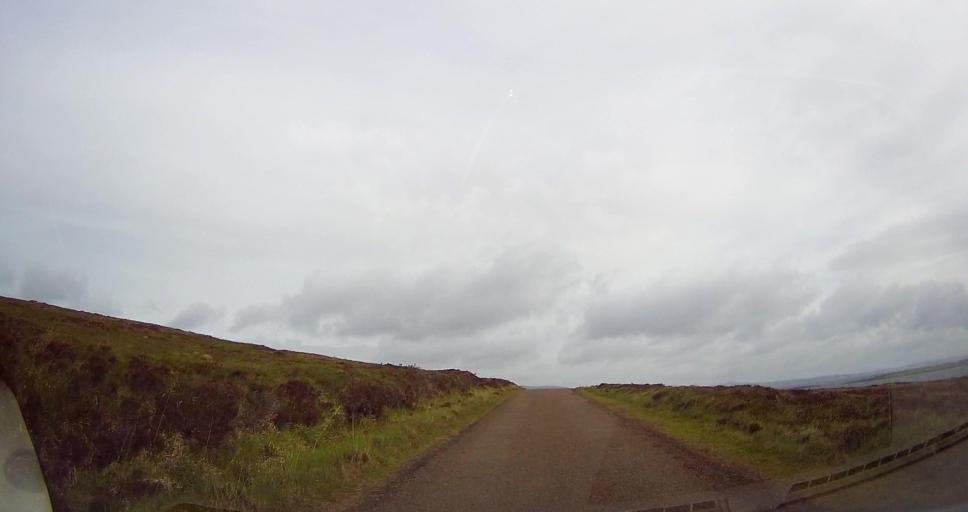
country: GB
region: Scotland
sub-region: Orkney Islands
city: Stromness
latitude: 58.8644
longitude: -3.2210
